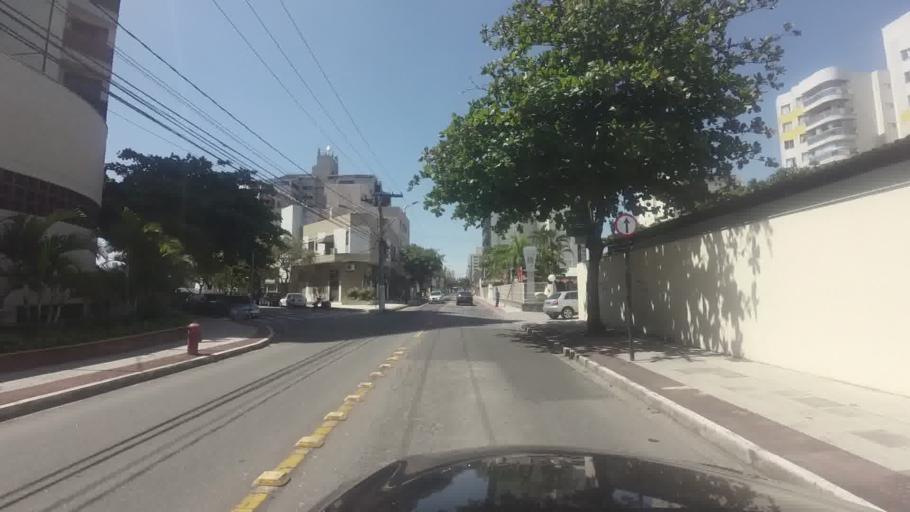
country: BR
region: Espirito Santo
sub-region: Vila Velha
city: Vila Velha
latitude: -20.2642
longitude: -40.2635
